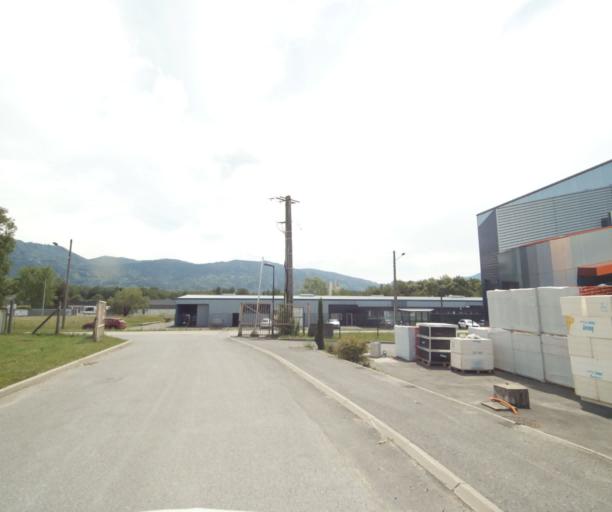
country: FR
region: Rhone-Alpes
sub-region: Departement de la Haute-Savoie
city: Perrignier
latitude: 46.3051
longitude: 6.4224
